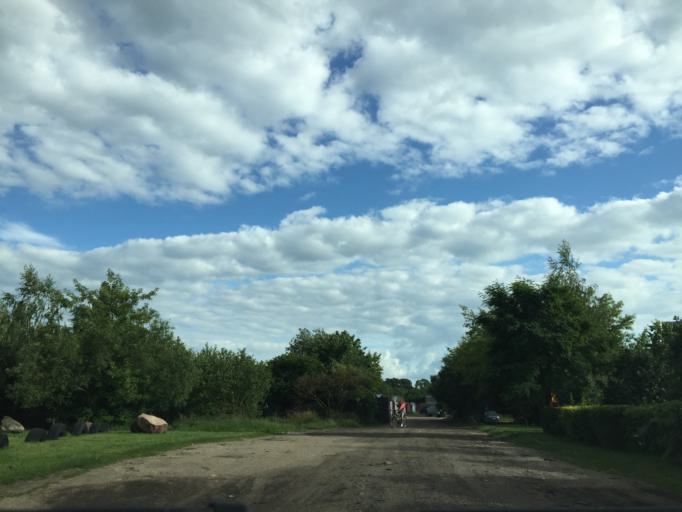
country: PL
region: Podlasie
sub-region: Suwalki
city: Suwalki
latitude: 54.1163
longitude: 22.9308
